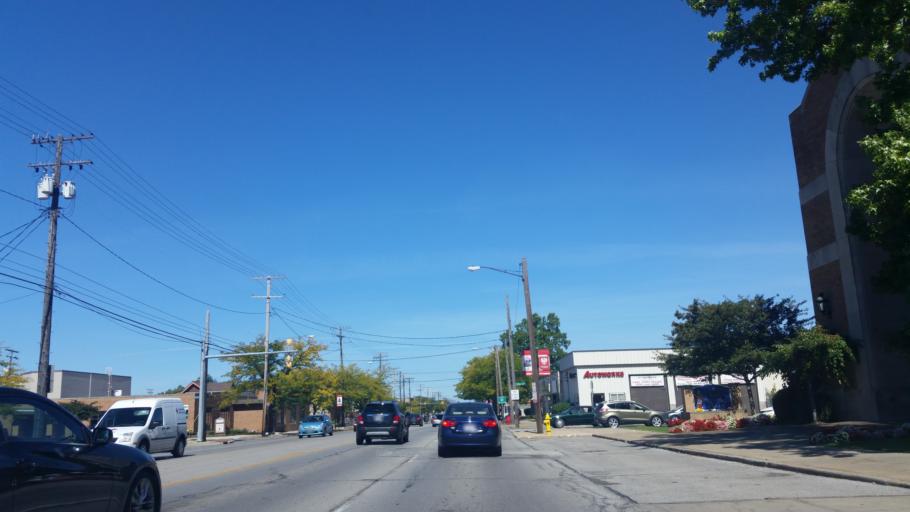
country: US
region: Ohio
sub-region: Cuyahoga County
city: Parma
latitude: 41.4025
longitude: -81.7344
